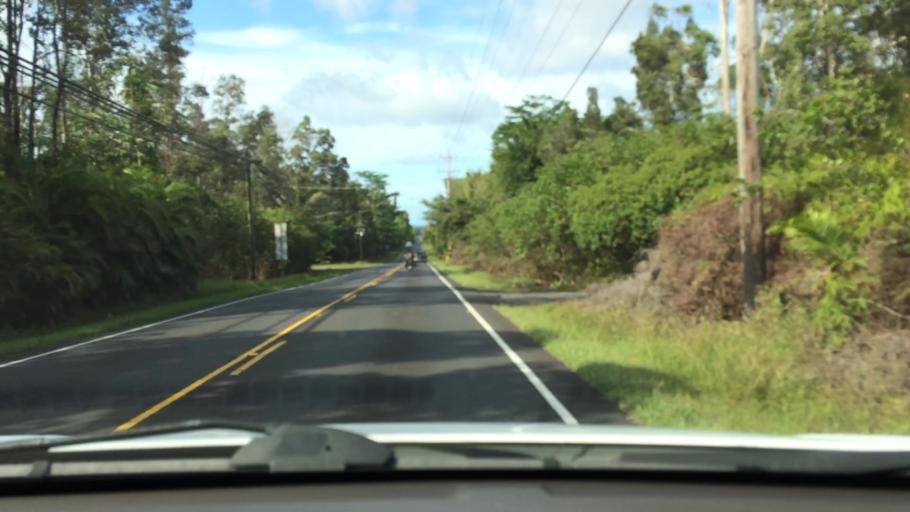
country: US
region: Hawaii
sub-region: Hawaii County
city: Hawaiian Paradise Park
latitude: 19.5085
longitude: -154.9471
